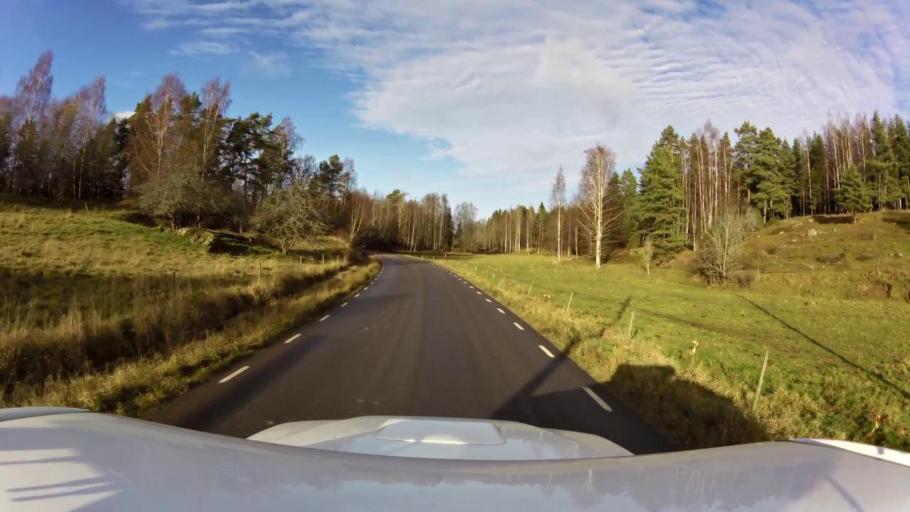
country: SE
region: OEstergoetland
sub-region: Linkopings Kommun
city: Sturefors
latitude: 58.3151
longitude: 15.6700
